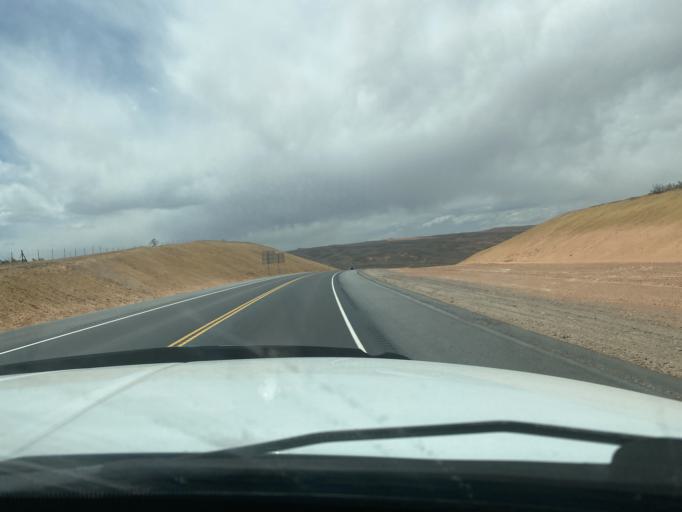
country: US
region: Utah
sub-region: Washington County
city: Hurricane
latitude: 37.1091
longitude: -113.3444
